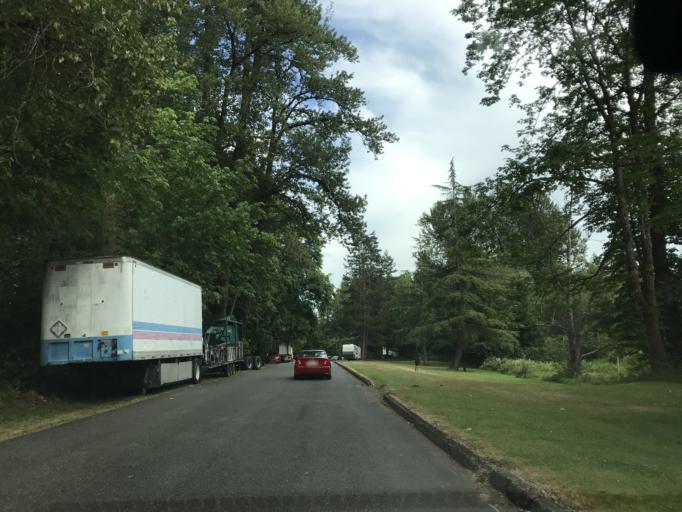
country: US
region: Washington
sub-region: King County
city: Maple Valley
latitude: 47.3770
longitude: -122.0423
